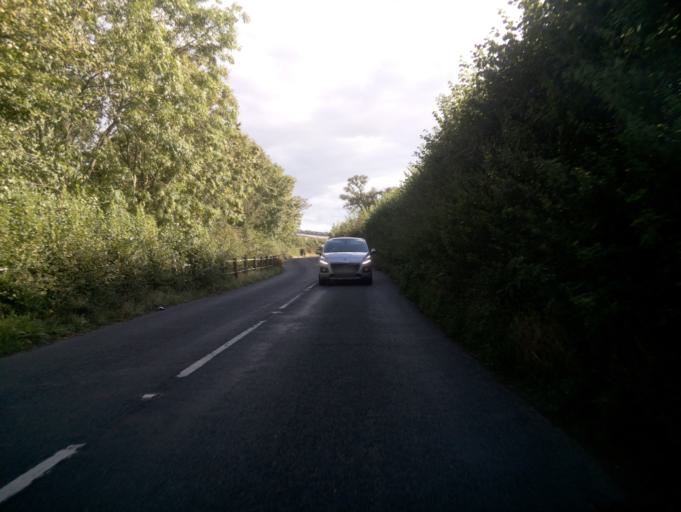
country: GB
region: England
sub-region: Devon
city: Sidmouth
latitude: 50.7115
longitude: -3.2241
